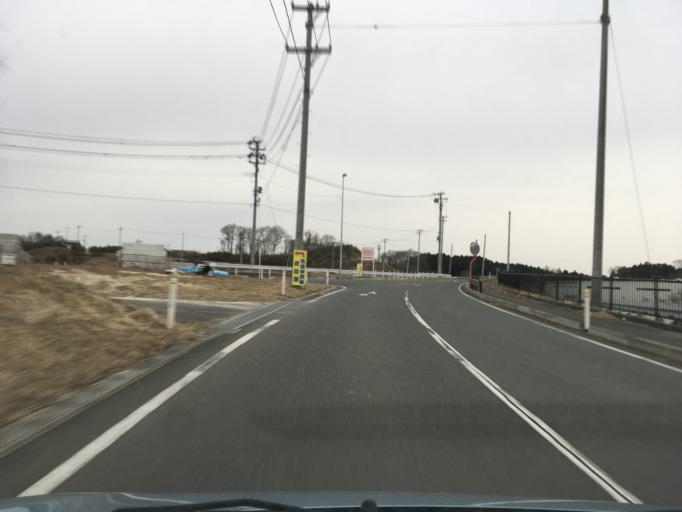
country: JP
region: Miyagi
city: Wakuya
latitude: 38.7000
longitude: 141.1699
